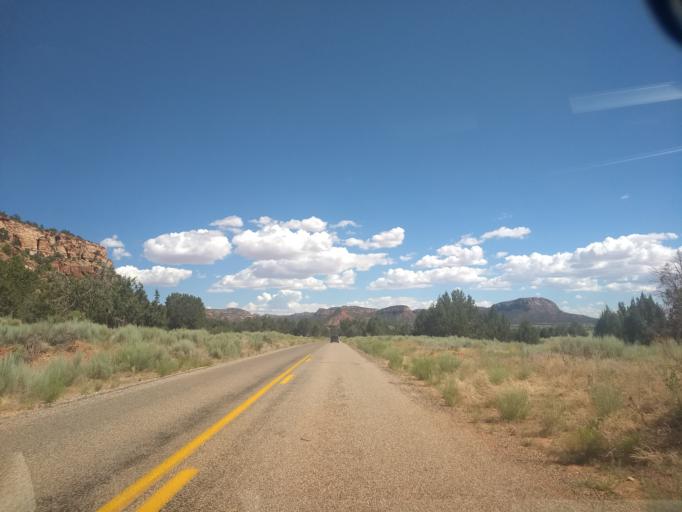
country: US
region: Utah
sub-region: Washington County
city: Hildale
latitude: 36.9690
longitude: -112.8715
